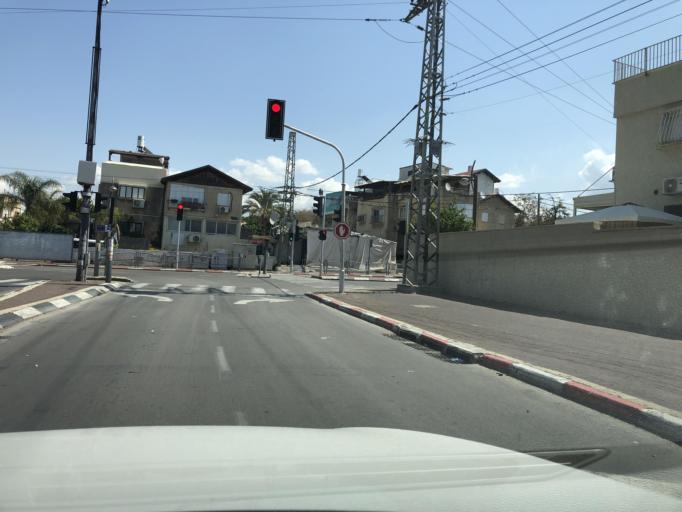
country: IL
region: Tel Aviv
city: Holon
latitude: 32.0060
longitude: 34.7643
